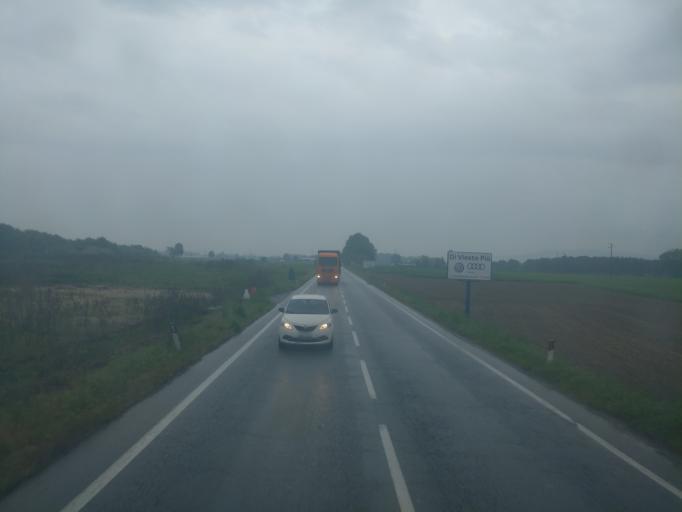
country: IT
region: Piedmont
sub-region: Provincia di Torino
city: Carignano
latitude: 44.9231
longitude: 7.6734
